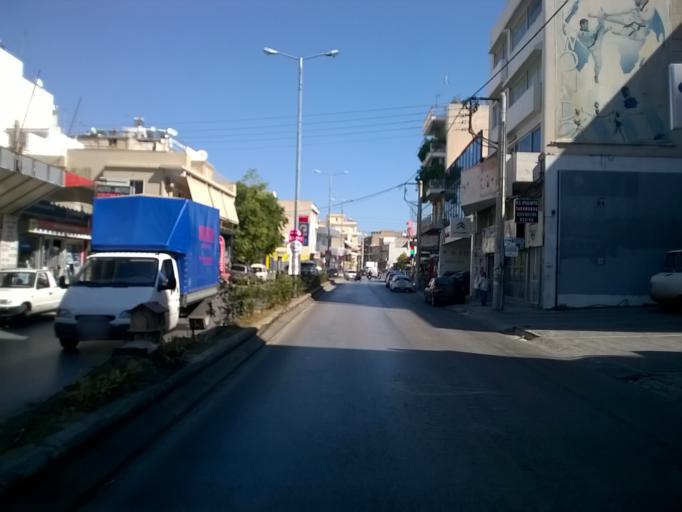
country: GR
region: Attica
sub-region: Nomos Piraios
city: Nikaia
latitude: 37.9603
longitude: 23.6554
